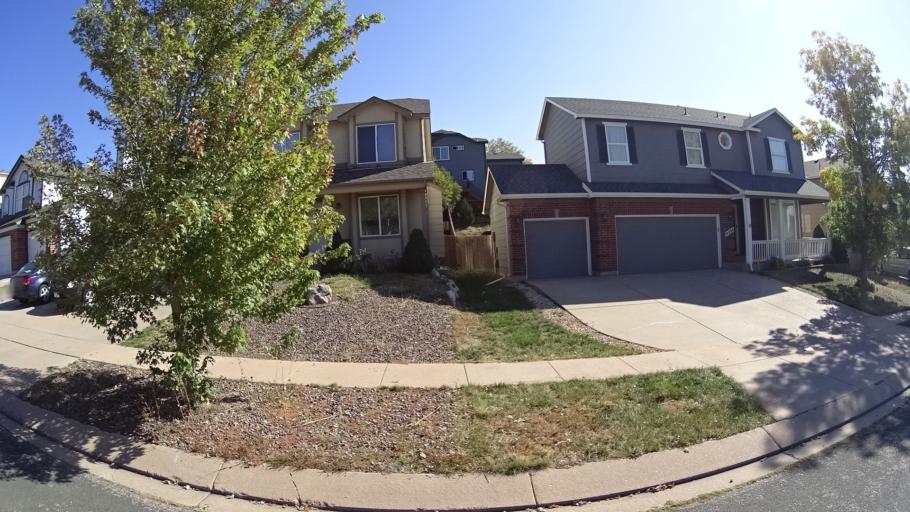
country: US
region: Colorado
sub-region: El Paso County
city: Cimarron Hills
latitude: 38.8816
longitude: -104.7048
